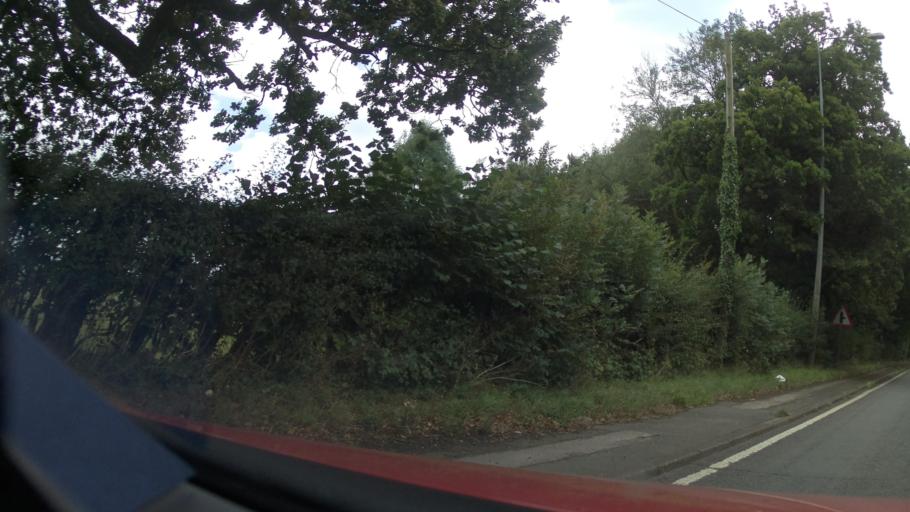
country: GB
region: England
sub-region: Staffordshire
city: Barlaston
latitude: 52.9467
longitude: -2.1899
